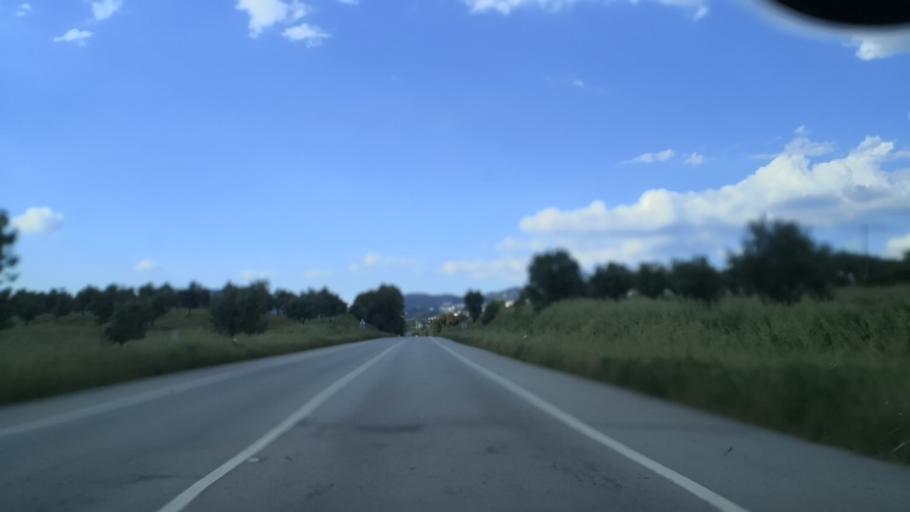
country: PT
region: Portalegre
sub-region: Portalegre
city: Portalegre
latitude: 39.2554
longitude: -7.4471
